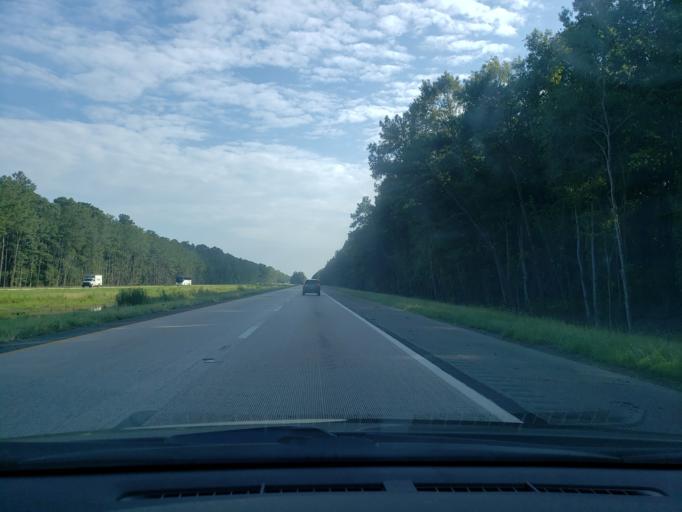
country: US
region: South Carolina
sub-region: Jasper County
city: Ridgeland
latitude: 32.4134
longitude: -81.0131
